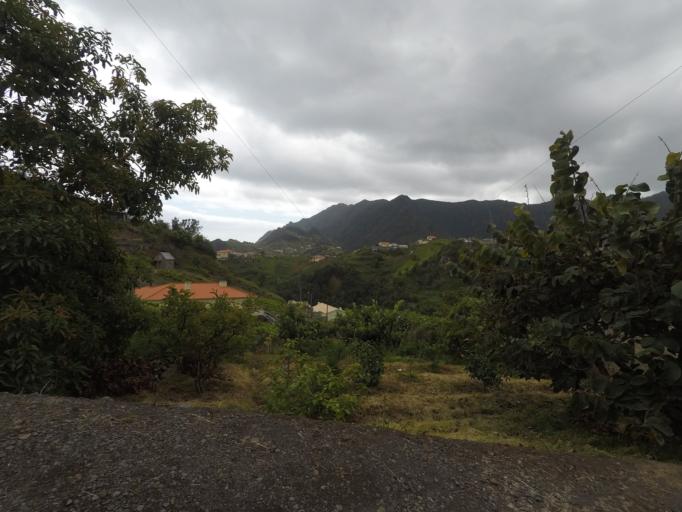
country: PT
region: Madeira
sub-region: Santana
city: Santana
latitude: 32.7676
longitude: -16.8315
